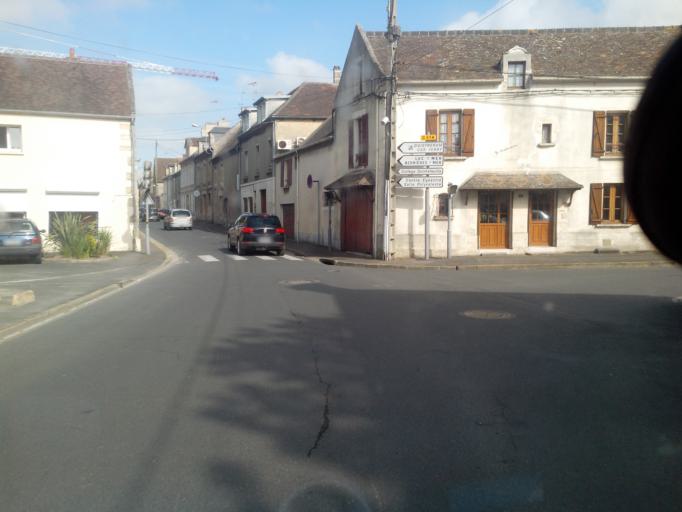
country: FR
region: Lower Normandy
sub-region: Departement du Calvados
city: Courseulles-sur-Mer
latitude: 49.3301
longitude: -0.4551
